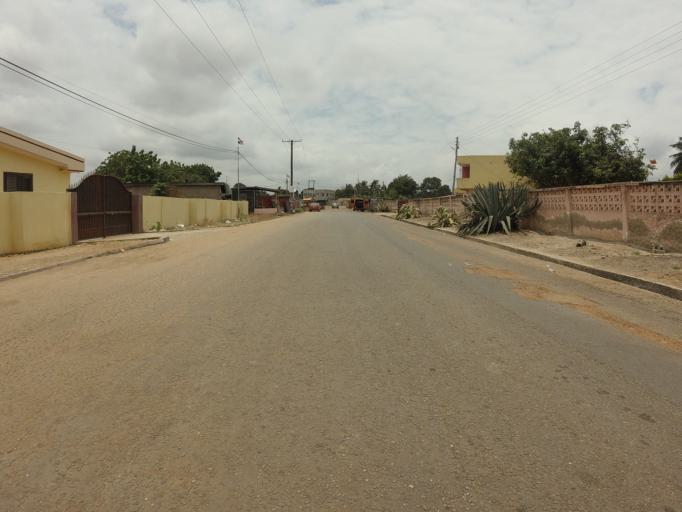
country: GH
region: Greater Accra
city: Nungua
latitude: 5.6160
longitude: -0.0787
